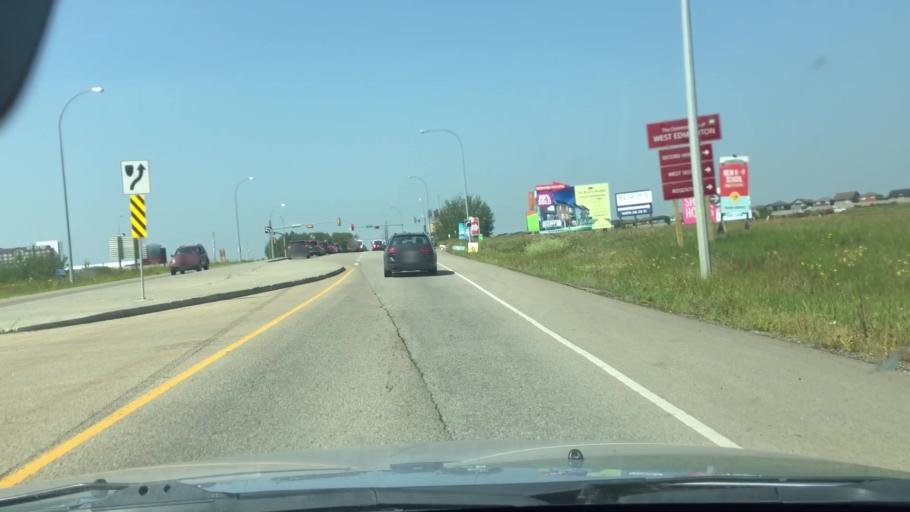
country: CA
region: Alberta
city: St. Albert
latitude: 53.5123
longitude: -113.6859
